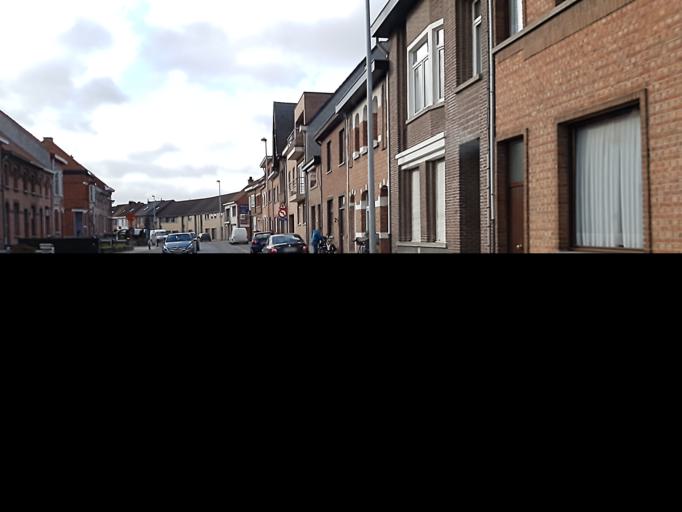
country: BE
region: Flanders
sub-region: Provincie Oost-Vlaanderen
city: Temse
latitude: 51.1287
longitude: 4.1968
